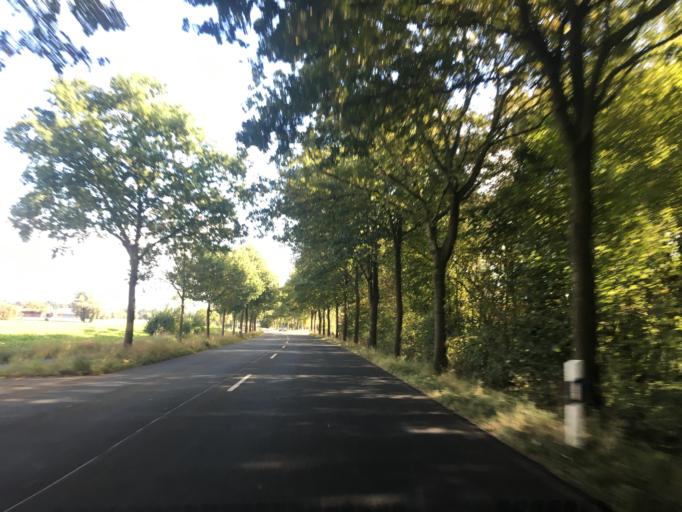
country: DE
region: North Rhine-Westphalia
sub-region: Regierungsbezirk Munster
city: Altenberge
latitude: 51.9966
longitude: 7.4953
